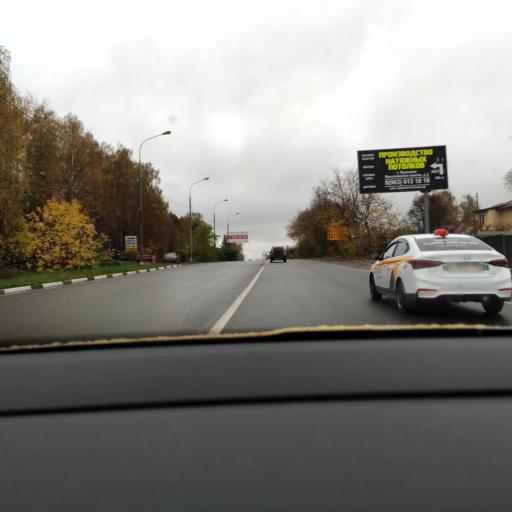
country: RU
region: Moskovskaya
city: Lesnyye Polyany
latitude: 55.9846
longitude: 37.8812
